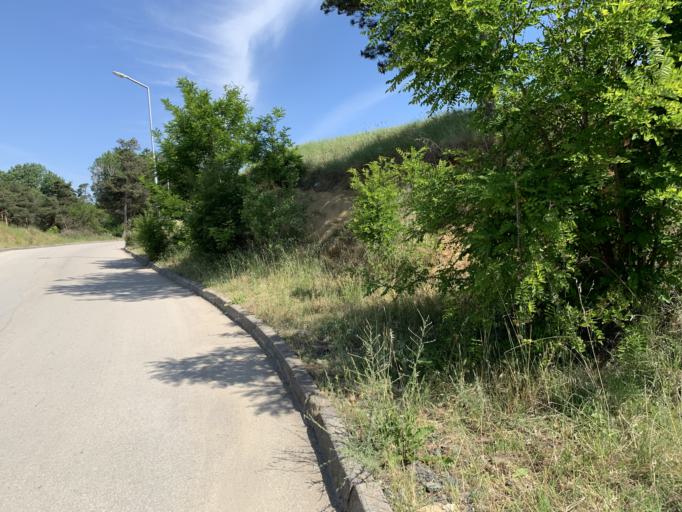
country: AL
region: Korce
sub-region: Rrethi i Korces
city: Korce
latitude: 40.6130
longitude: 20.7902
